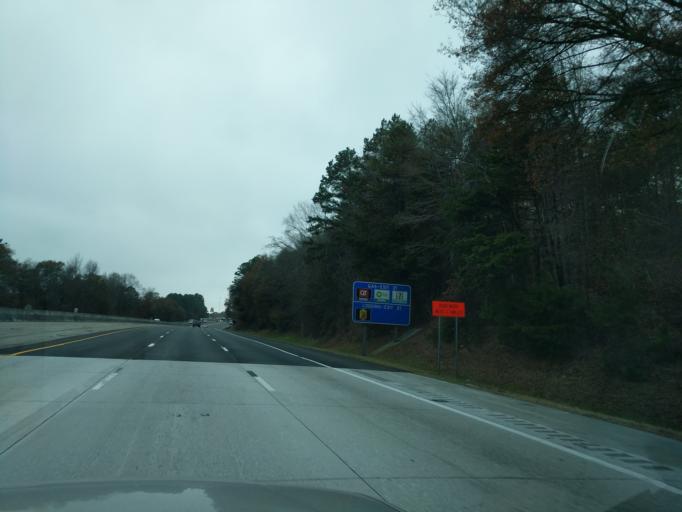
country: US
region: South Carolina
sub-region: Anderson County
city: Northlake
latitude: 34.5828
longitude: -82.6847
